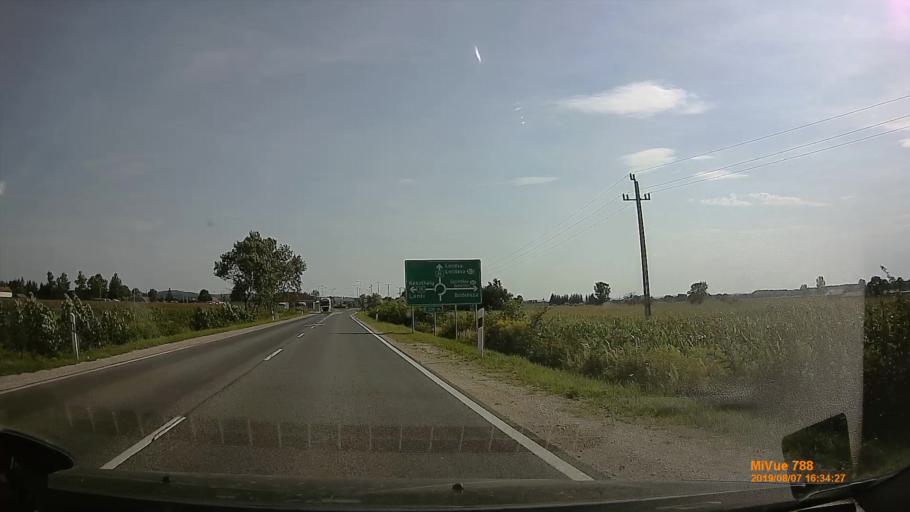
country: SI
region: Lendava-Lendva
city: Lendava
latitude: 46.6208
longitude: 16.4655
